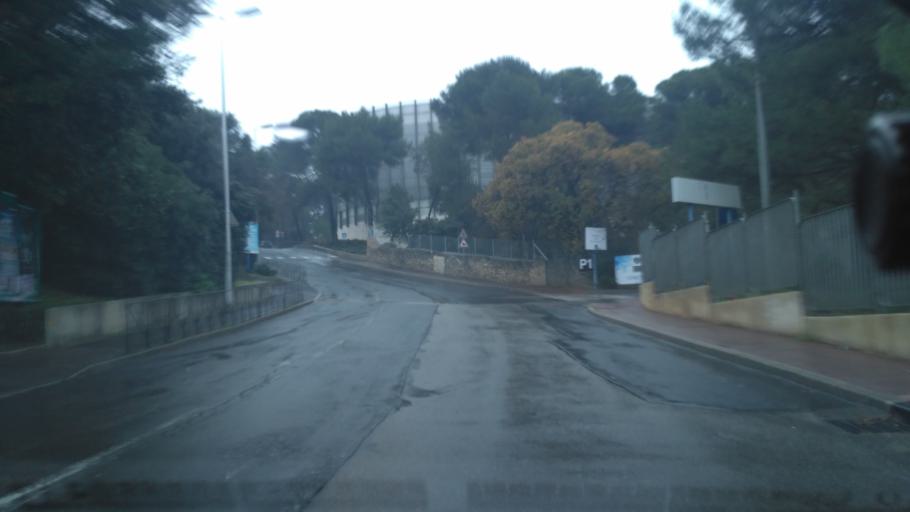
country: FR
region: Languedoc-Roussillon
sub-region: Departement de l'Herault
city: Clapiers
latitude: 43.6383
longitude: 3.8739
